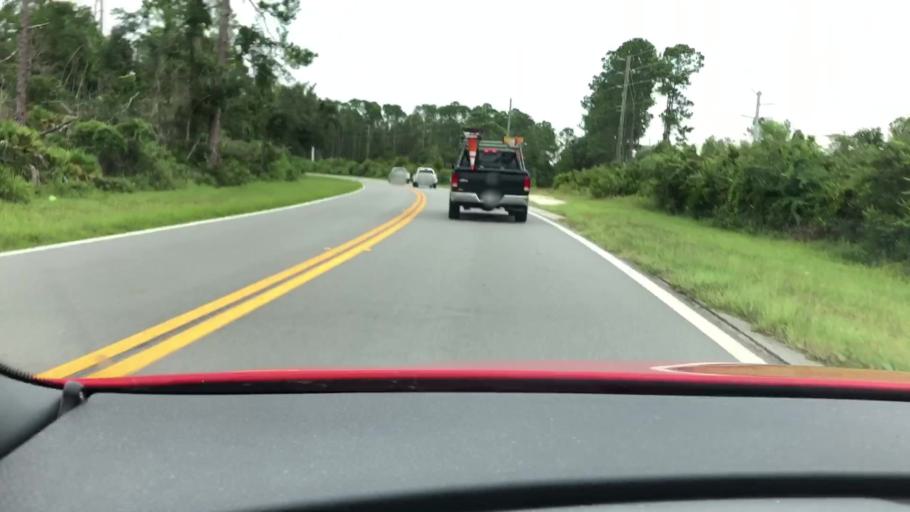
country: US
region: Florida
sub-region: Flagler County
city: Palm Coast
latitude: 29.5109
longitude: -81.1948
